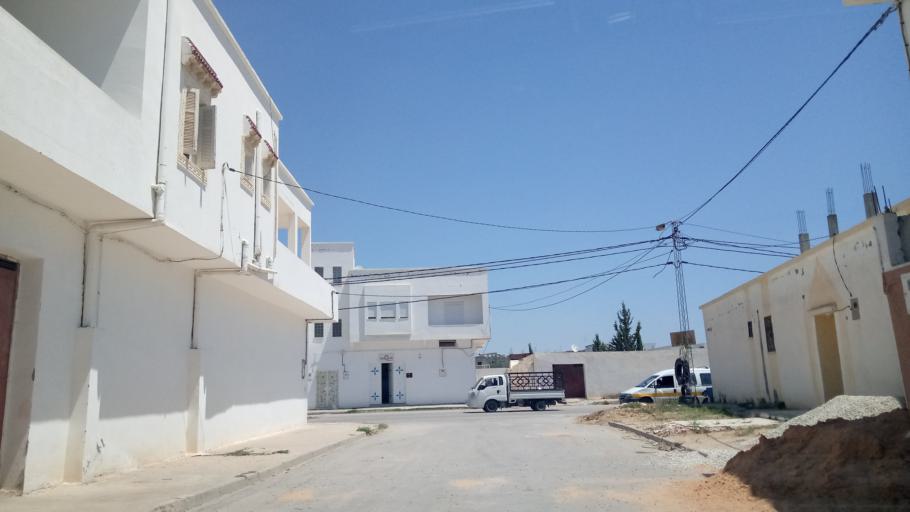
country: TN
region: Al Qayrawan
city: Sbikha
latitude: 36.1192
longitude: 10.0910
